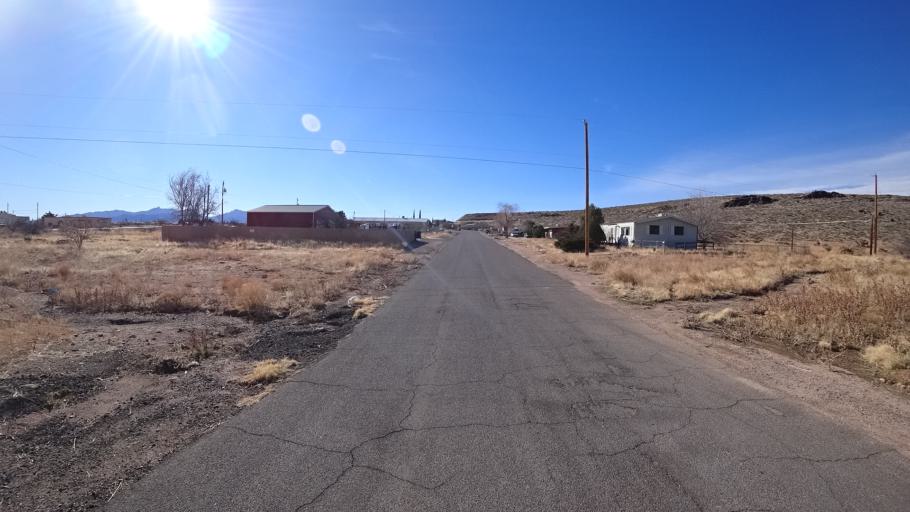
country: US
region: Arizona
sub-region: Mohave County
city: New Kingman-Butler
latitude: 35.2587
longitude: -114.0395
